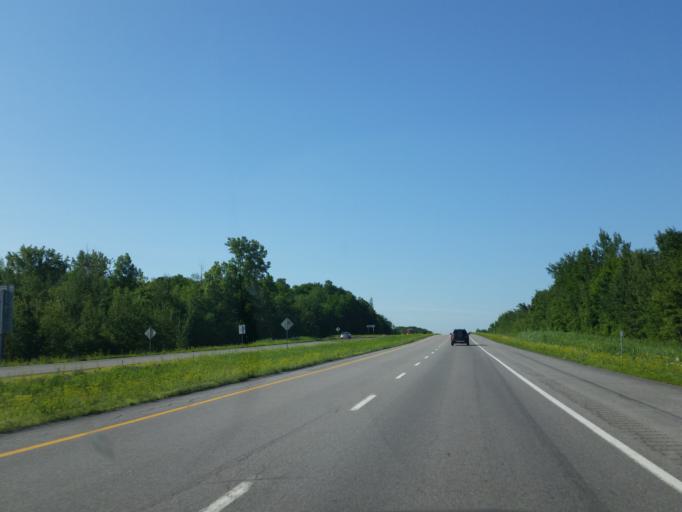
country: CA
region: Quebec
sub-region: Monteregie
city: Napierville
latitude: 45.2603
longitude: -73.4692
